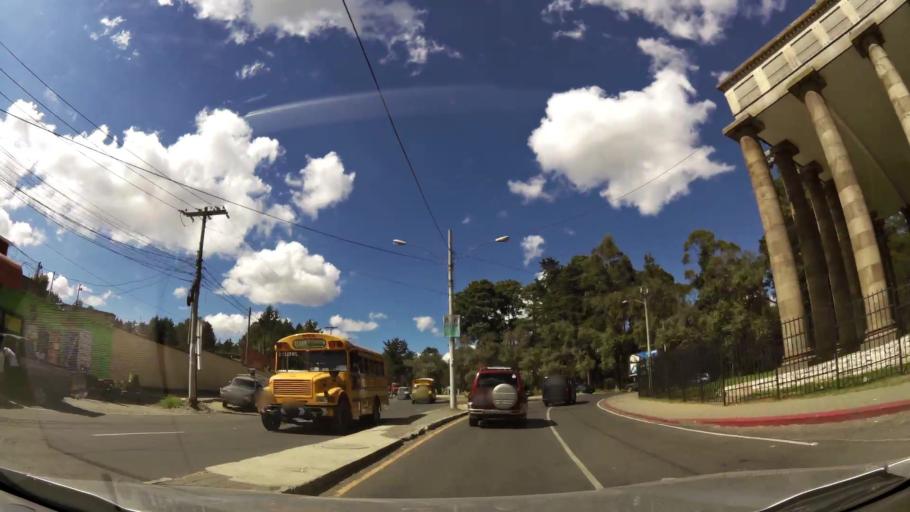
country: GT
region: Quetzaltenango
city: Quetzaltenango
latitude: 14.8458
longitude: -91.5338
